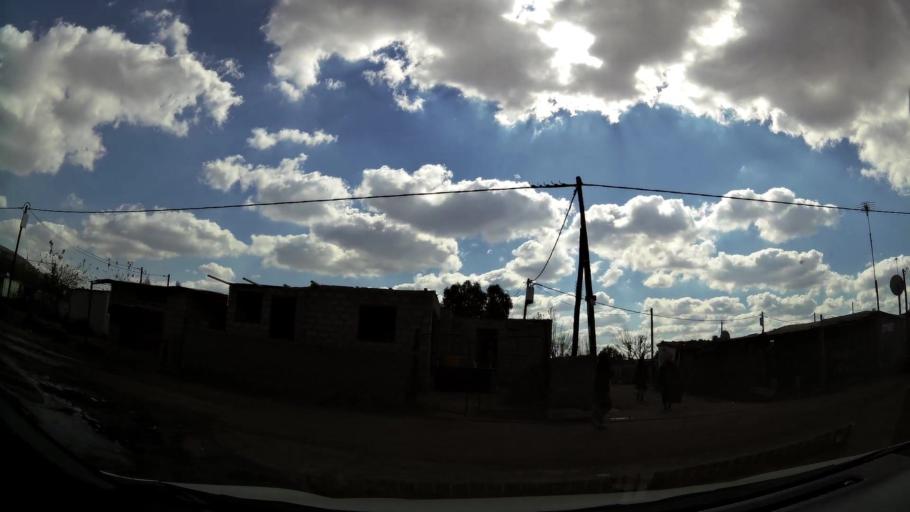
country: ZA
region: Gauteng
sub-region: City of Tshwane Metropolitan Municipality
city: Cullinan
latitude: -25.7008
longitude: 28.4021
